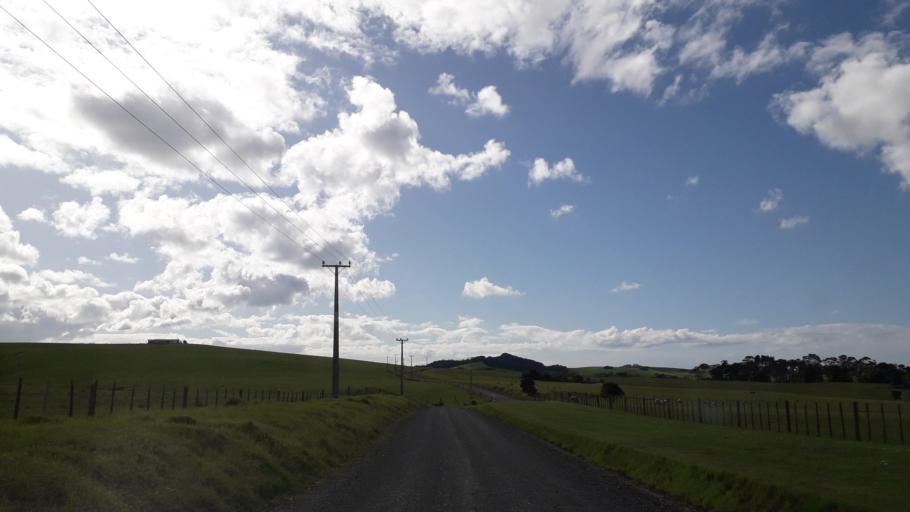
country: NZ
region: Northland
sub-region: Far North District
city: Kerikeri
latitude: -35.1512
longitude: 174.0400
